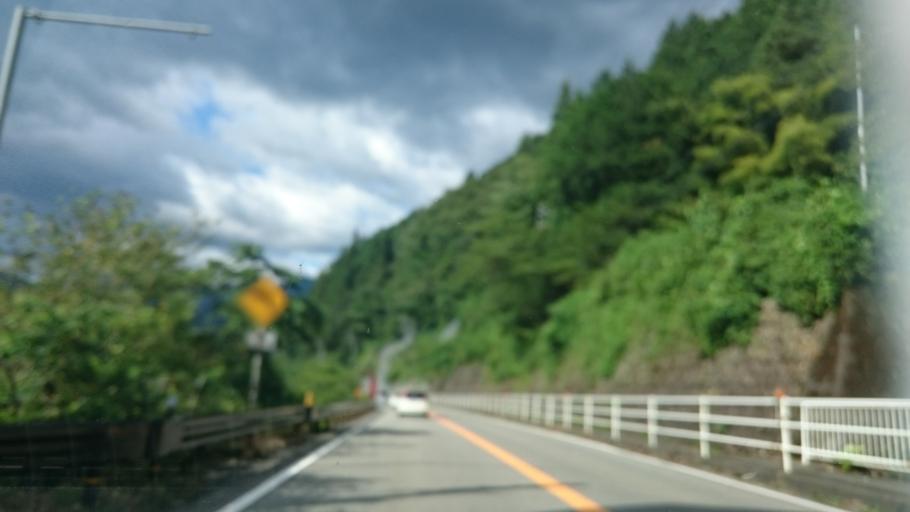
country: JP
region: Gifu
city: Gujo
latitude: 35.7836
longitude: 137.2546
